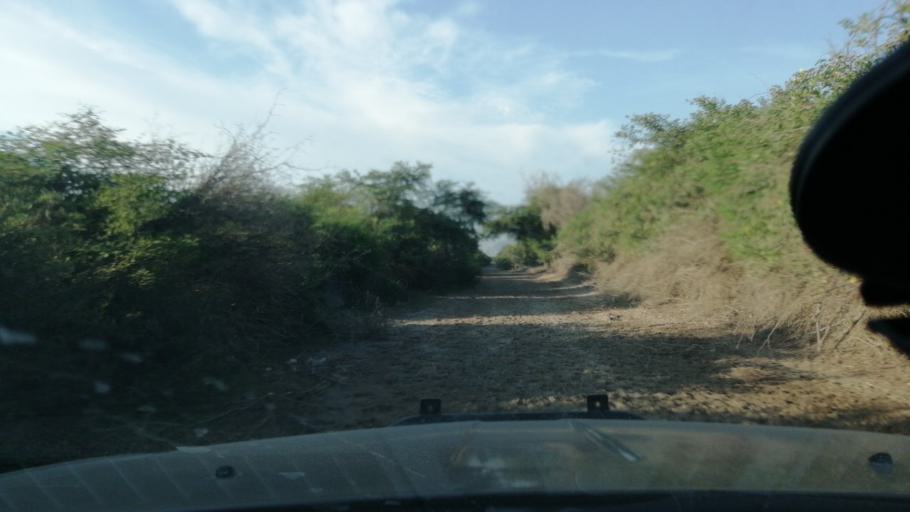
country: PE
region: Ica
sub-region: Provincia de Chincha
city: San Pedro
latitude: -13.3509
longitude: -76.1633
